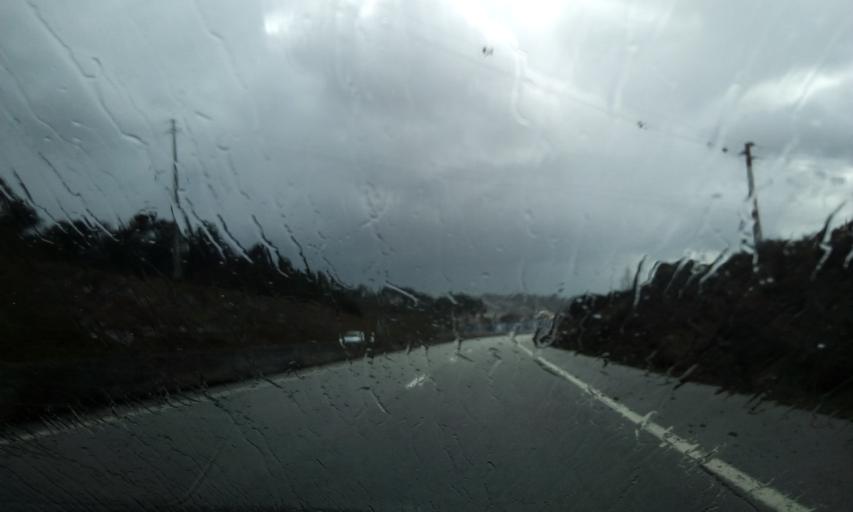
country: PT
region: Viseu
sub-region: Viseu
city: Viseu
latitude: 40.6242
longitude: -7.9104
